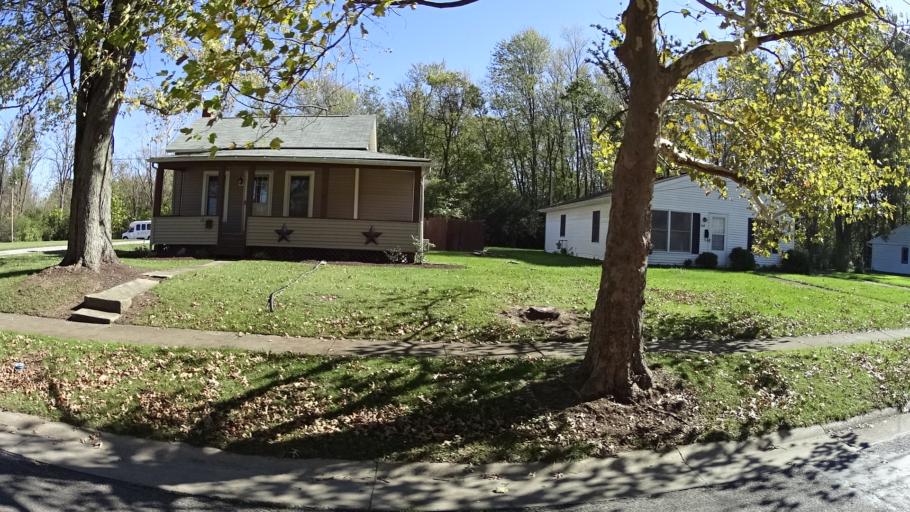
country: US
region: Ohio
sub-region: Lorain County
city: Oberlin
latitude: 41.2884
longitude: -82.2126
